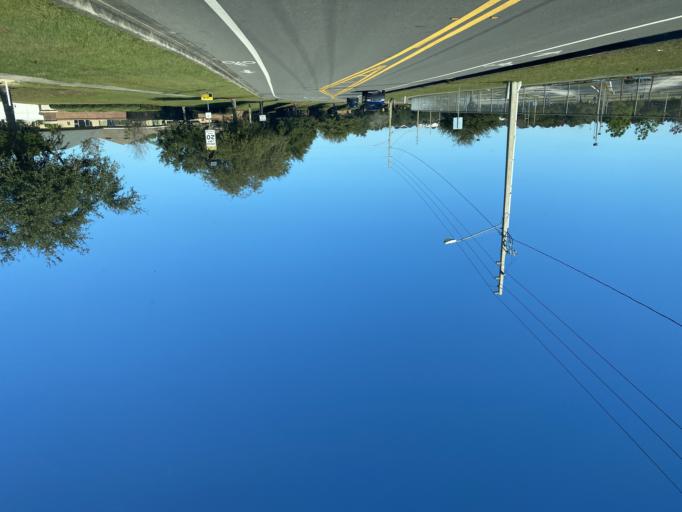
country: US
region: Florida
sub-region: Lake County
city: Minneola
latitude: 28.5253
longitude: -81.7206
